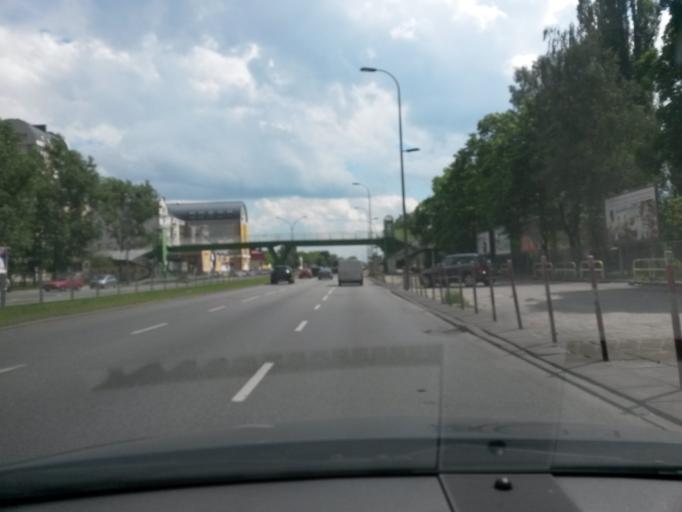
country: PL
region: Masovian Voivodeship
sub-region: Warszawa
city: Mokotow
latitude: 52.1910
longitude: 21.0589
